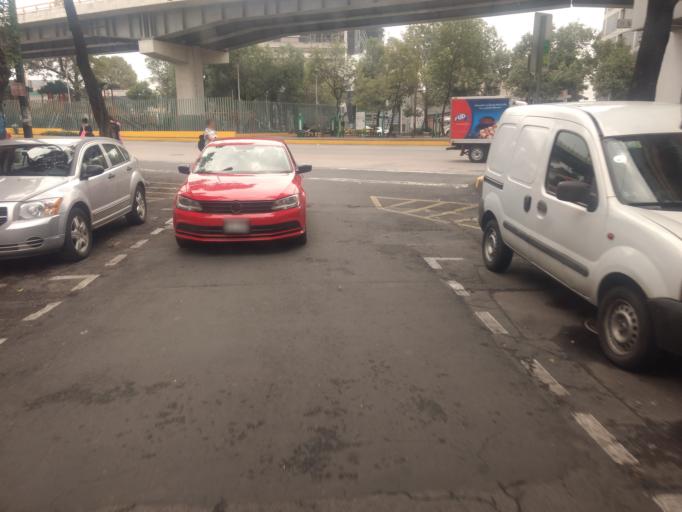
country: MX
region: Mexico City
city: Alvaro Obregon
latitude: 19.3716
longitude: -99.1870
